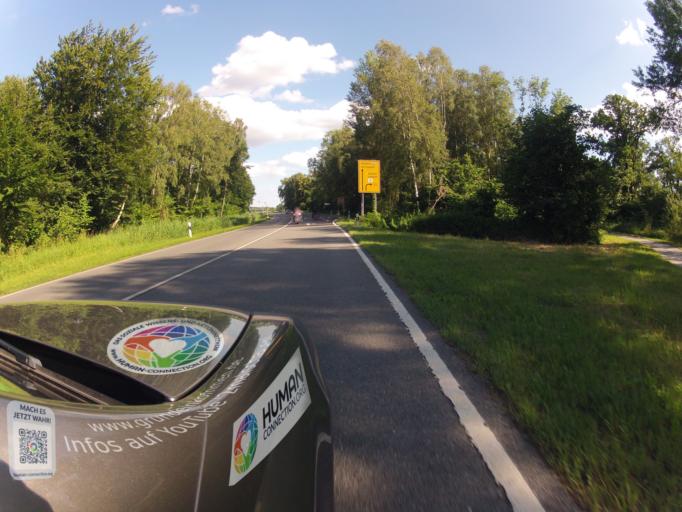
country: DE
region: Mecklenburg-Vorpommern
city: Seebad Bansin
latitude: 53.9843
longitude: 14.0758
